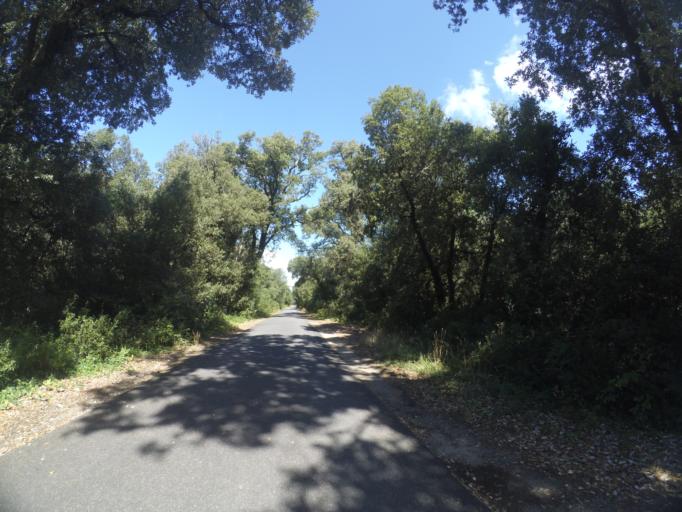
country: FR
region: Poitou-Charentes
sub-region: Departement de la Charente-Maritime
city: Les Mathes
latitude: 45.6720
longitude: -1.1485
